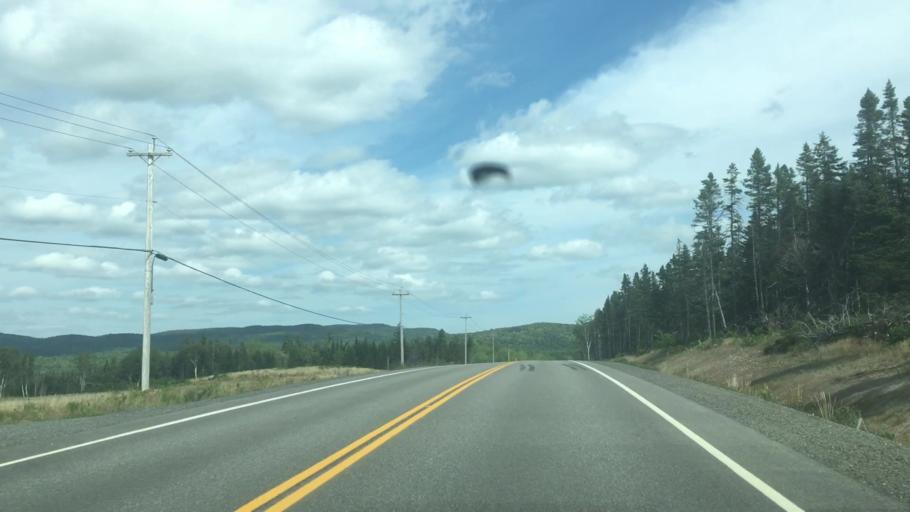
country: CA
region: Nova Scotia
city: Sydney Mines
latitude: 46.3302
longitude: -60.6016
